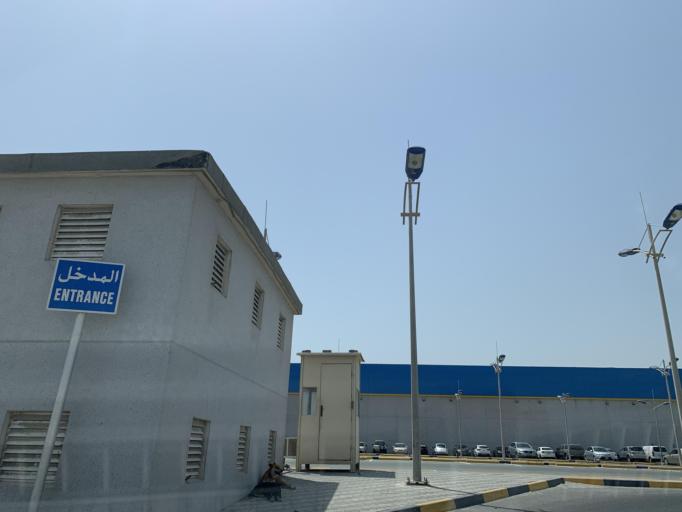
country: BH
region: Northern
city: Madinat `Isa
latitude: 26.1948
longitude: 50.5413
